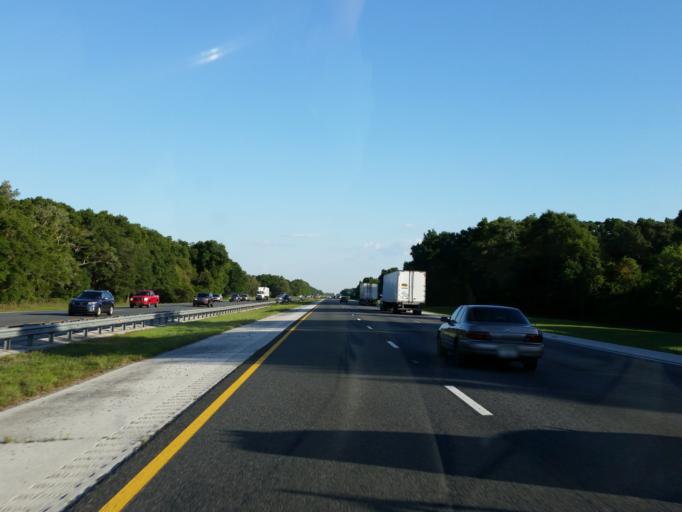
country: US
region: Florida
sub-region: Marion County
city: Ocala
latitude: 29.2948
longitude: -82.2033
